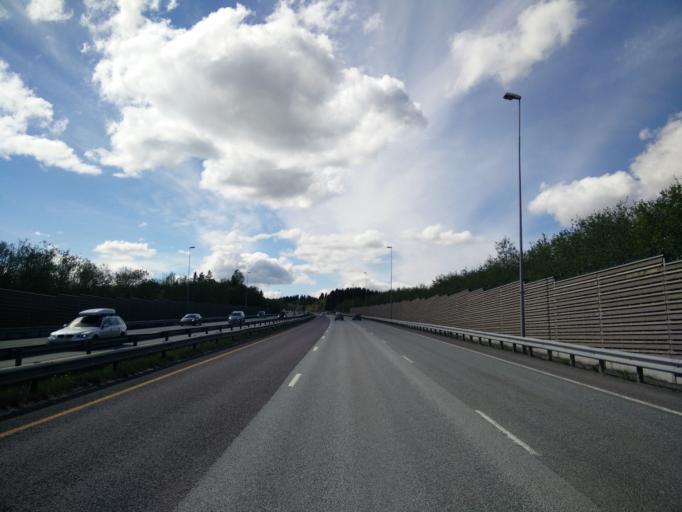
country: NO
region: Sor-Trondelag
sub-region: Trondheim
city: Trondheim
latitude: 63.3878
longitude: 10.3793
